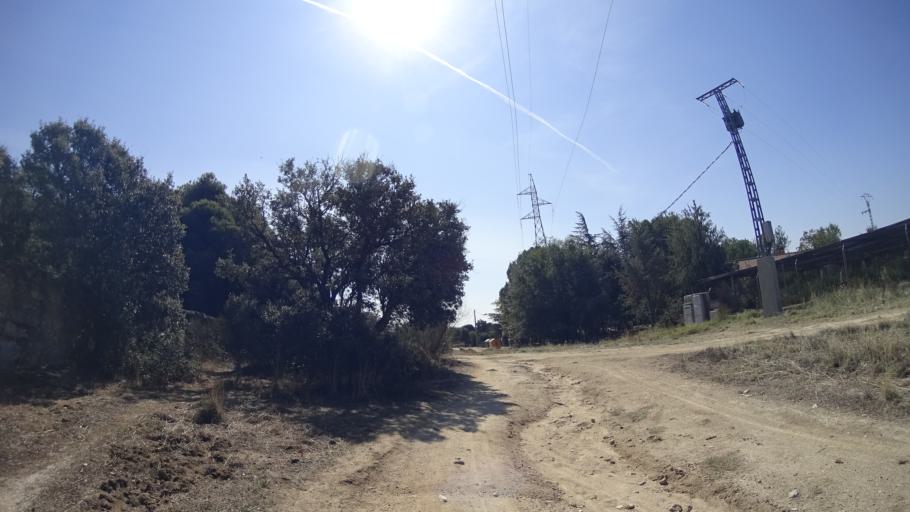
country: ES
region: Madrid
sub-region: Provincia de Madrid
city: Colmenarejo
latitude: 40.5727
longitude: -4.0255
